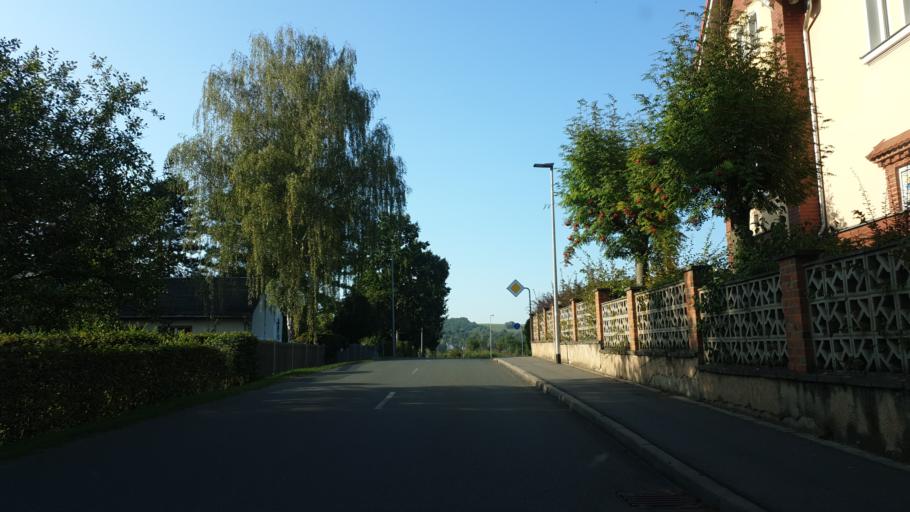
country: DE
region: Thuringia
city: Hartmannsdorf
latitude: 50.9633
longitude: 11.9773
